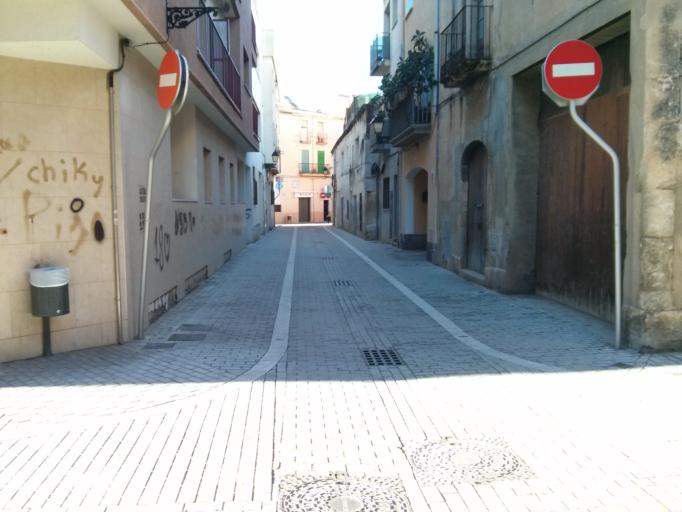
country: ES
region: Catalonia
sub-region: Provincia de Tarragona
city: El Vendrell
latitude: 41.2229
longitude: 1.5344
